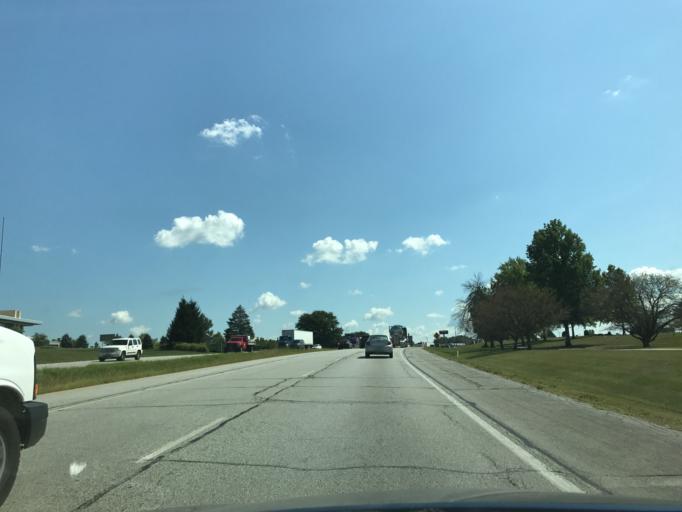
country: US
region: Indiana
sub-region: Porter County
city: Valparaiso
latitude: 41.4604
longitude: -87.0426
